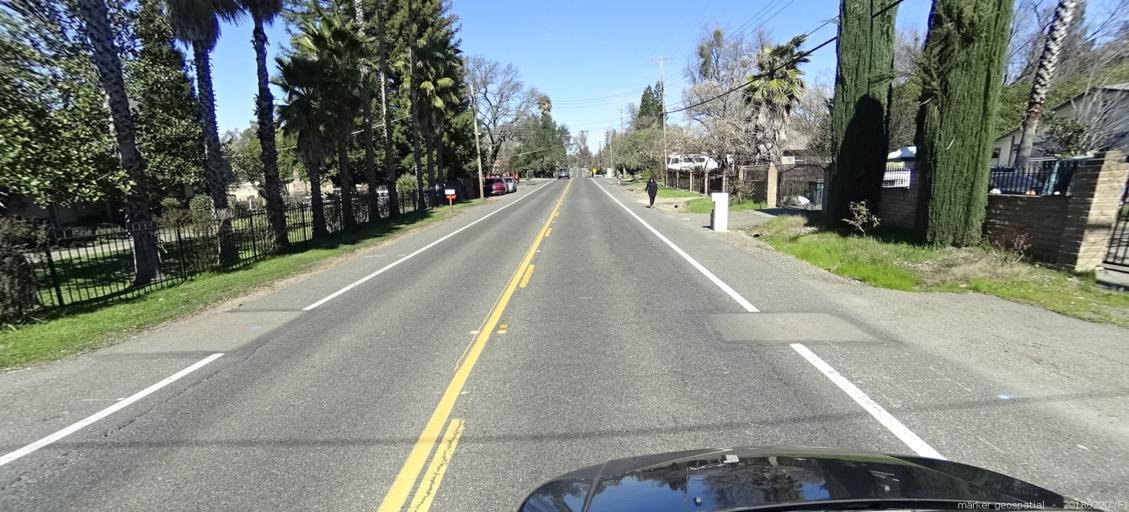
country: US
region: California
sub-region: Sacramento County
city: Orangevale
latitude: 38.6877
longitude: -121.2349
